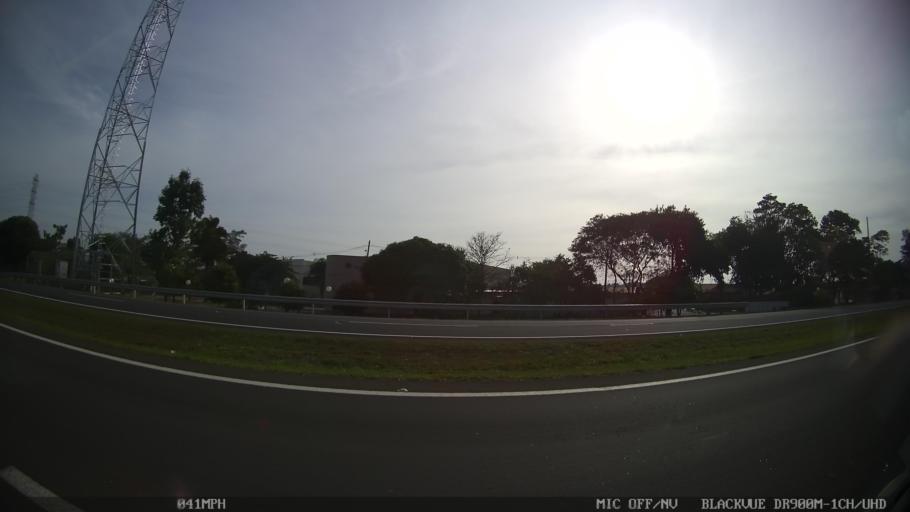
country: BR
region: Sao Paulo
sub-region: Piracicaba
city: Piracicaba
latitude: -22.6792
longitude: -47.7108
